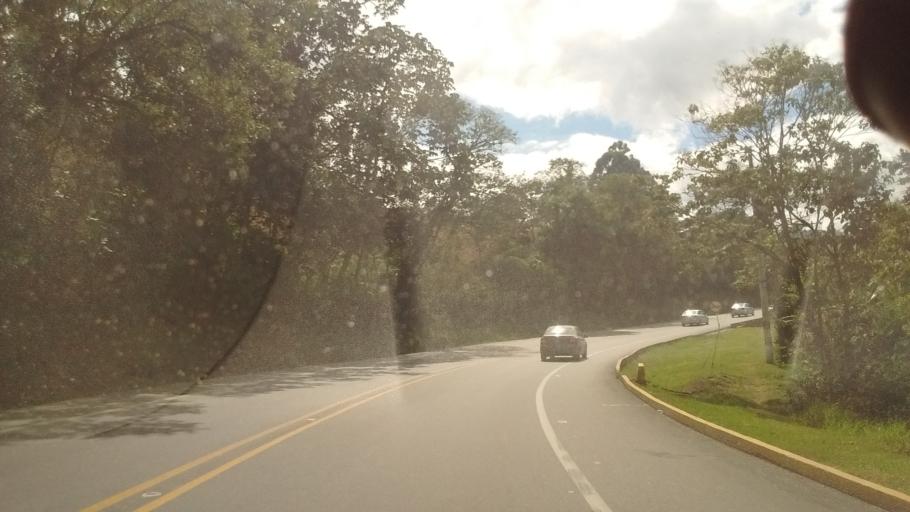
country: CO
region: Cauca
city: Cajibio
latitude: 2.6102
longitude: -76.5269
